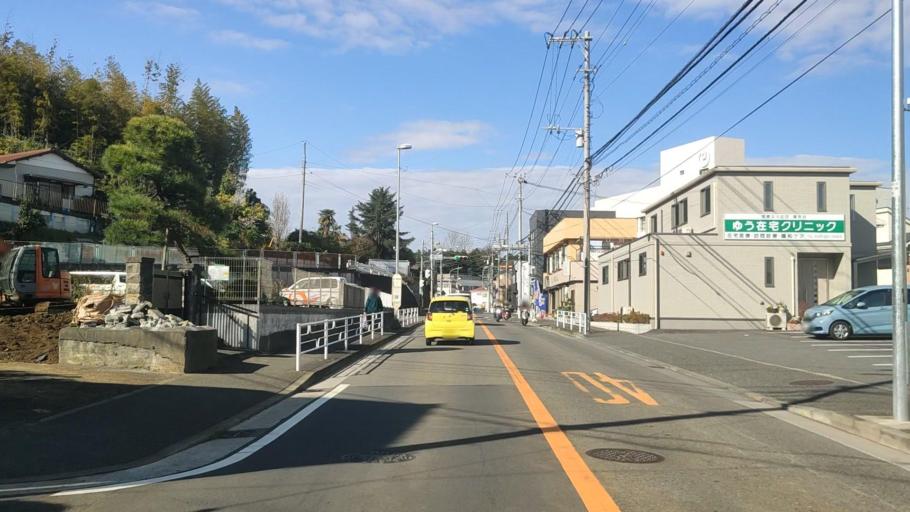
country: JP
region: Kanagawa
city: Yokohama
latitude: 35.4499
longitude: 139.5582
